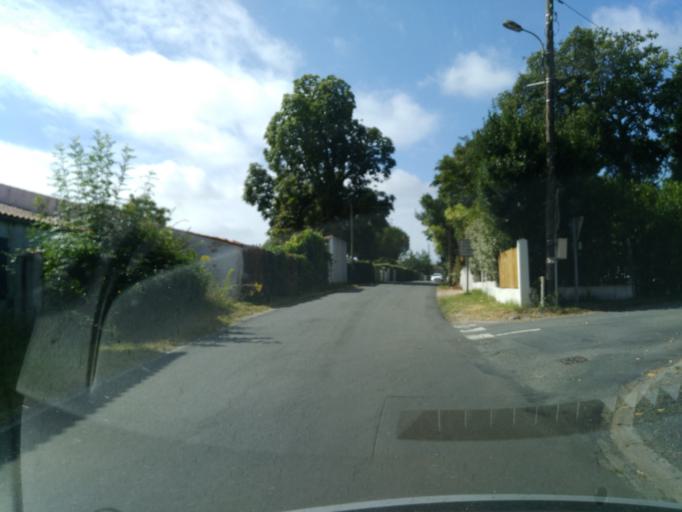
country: FR
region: Poitou-Charentes
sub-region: Departement de la Charente-Maritime
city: Breuillet
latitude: 45.6914
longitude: -1.0700
